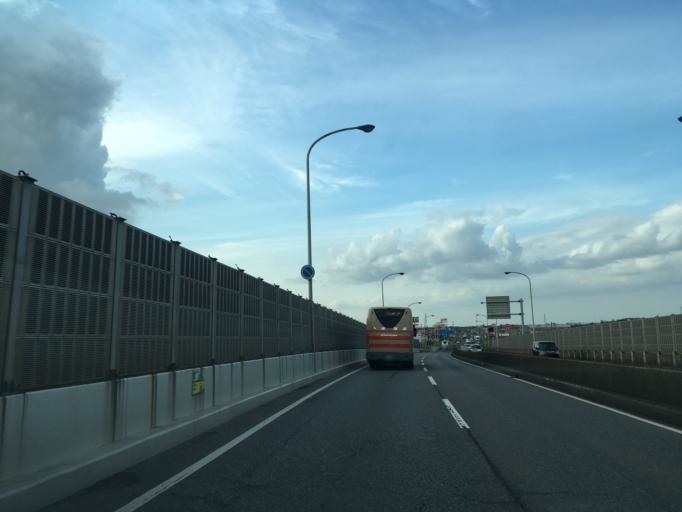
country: JP
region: Chiba
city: Kisarazu
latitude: 35.3910
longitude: 139.9409
